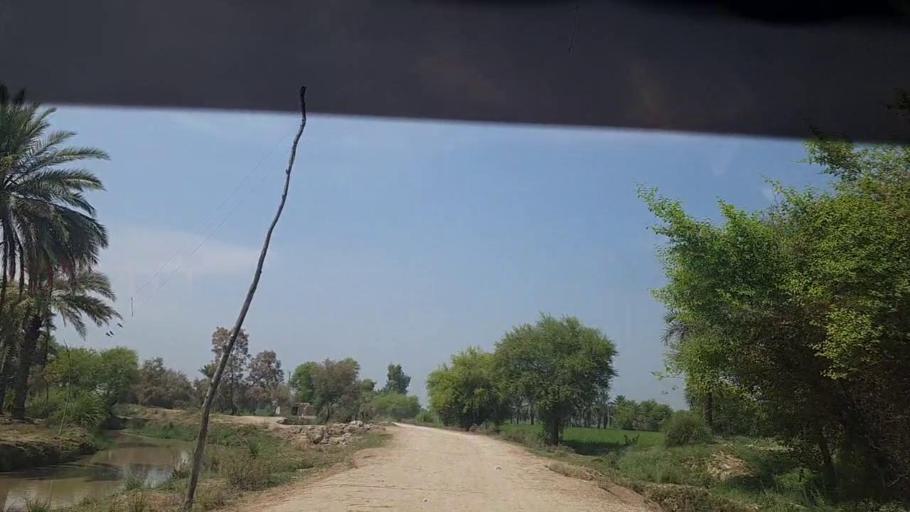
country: PK
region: Sindh
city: Thul
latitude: 28.2032
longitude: 68.6970
